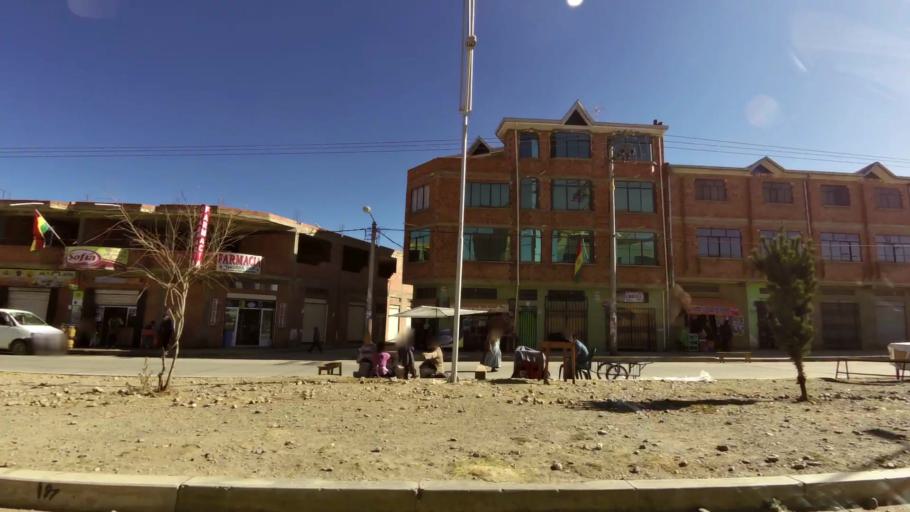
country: BO
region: La Paz
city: La Paz
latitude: -16.5284
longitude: -68.2295
